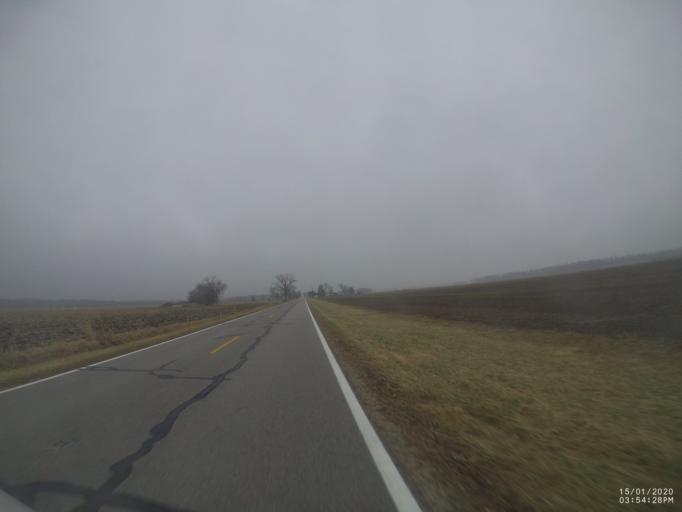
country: US
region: Ohio
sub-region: Sandusky County
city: Woodville
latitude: 41.4137
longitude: -83.4015
